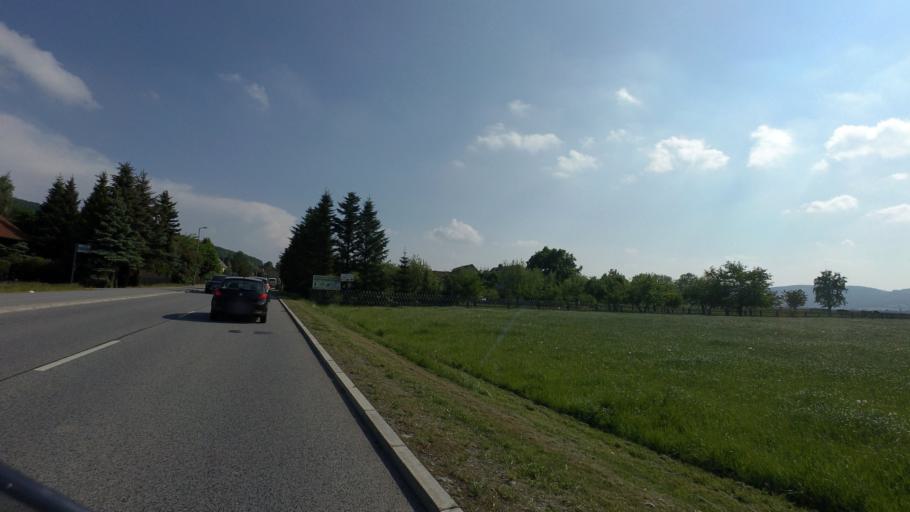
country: DE
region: Saxony
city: Grosspostwitz
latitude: 51.1423
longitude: 14.4409
